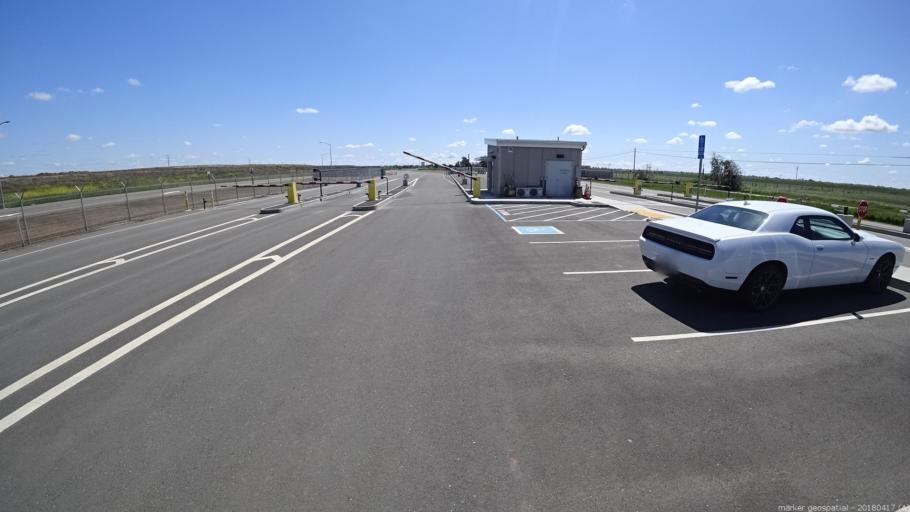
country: US
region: California
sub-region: Sacramento County
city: Laguna
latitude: 38.4429
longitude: -121.4633
